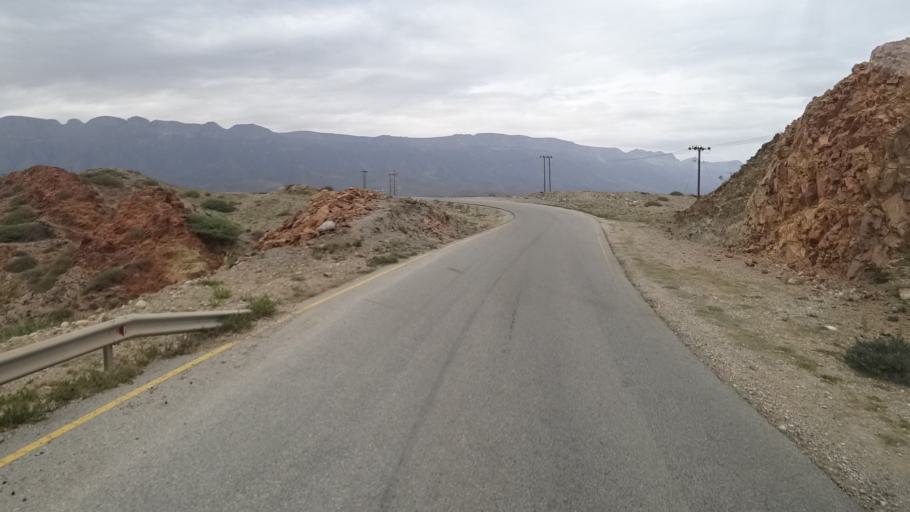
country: OM
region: Zufar
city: Salalah
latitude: 17.1515
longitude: 55.0055
